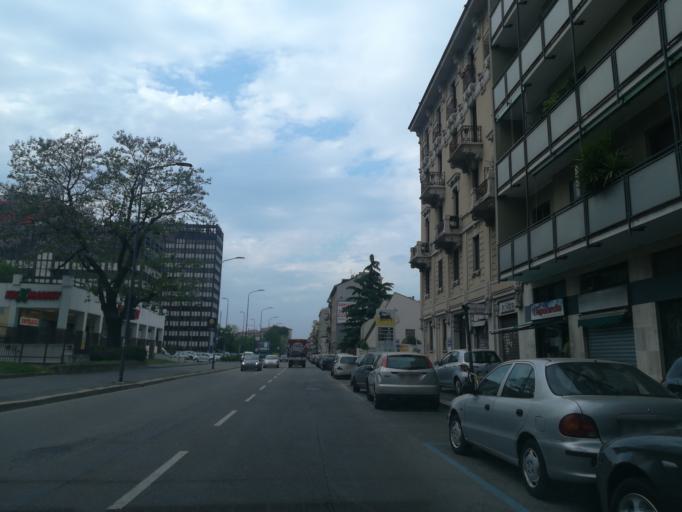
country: IT
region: Lombardy
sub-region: Citta metropolitana di Milano
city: Milano
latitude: 45.4974
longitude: 9.1917
